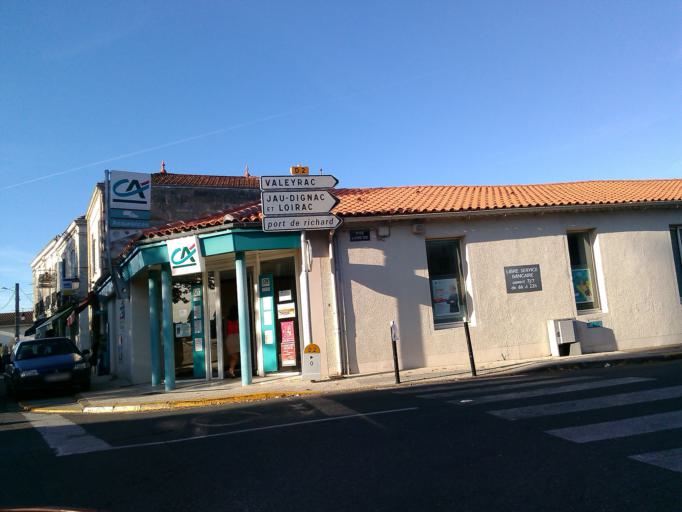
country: FR
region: Aquitaine
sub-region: Departement de la Gironde
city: Soulac-sur-Mer
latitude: 45.4306
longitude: -1.0351
